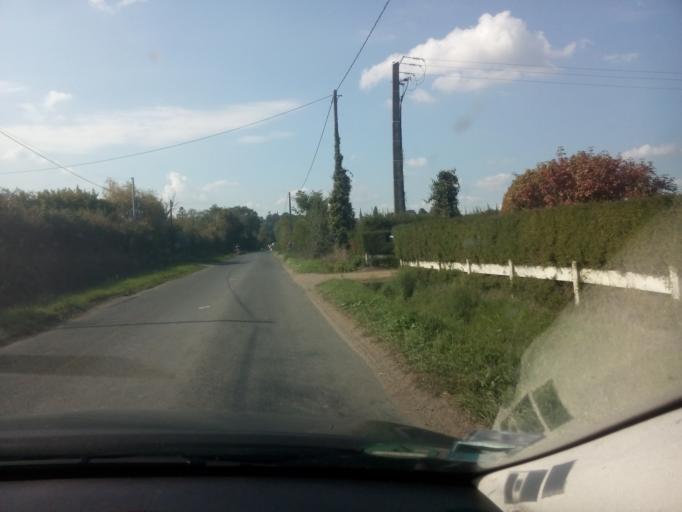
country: FR
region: Pays de la Loire
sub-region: Departement de Maine-et-Loire
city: Soulaire-et-Bourg
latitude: 47.5757
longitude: -0.5379
